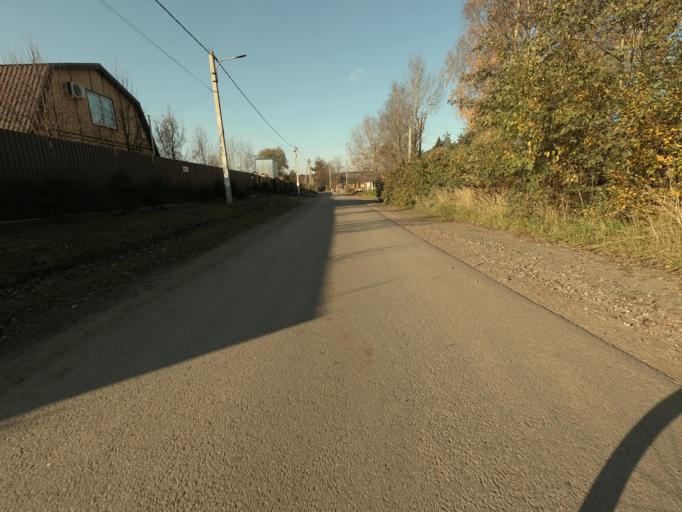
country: RU
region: Leningrad
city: Luppolovo
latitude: 60.1370
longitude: 30.2559
